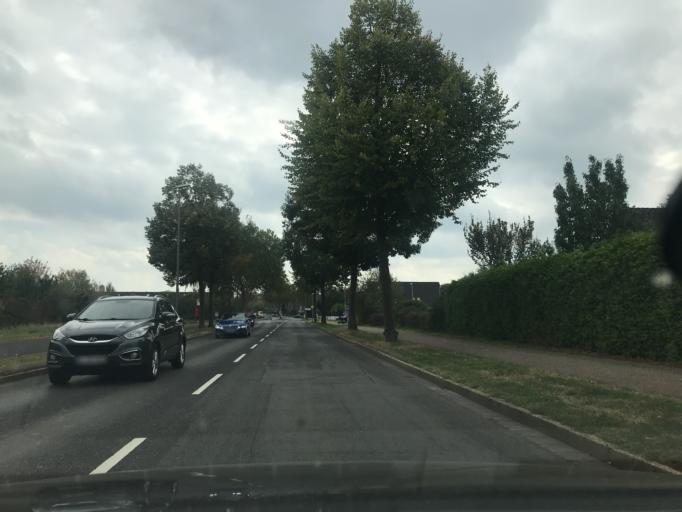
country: DE
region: North Rhine-Westphalia
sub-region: Regierungsbezirk Dusseldorf
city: Krefeld
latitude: 51.3700
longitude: 6.6363
